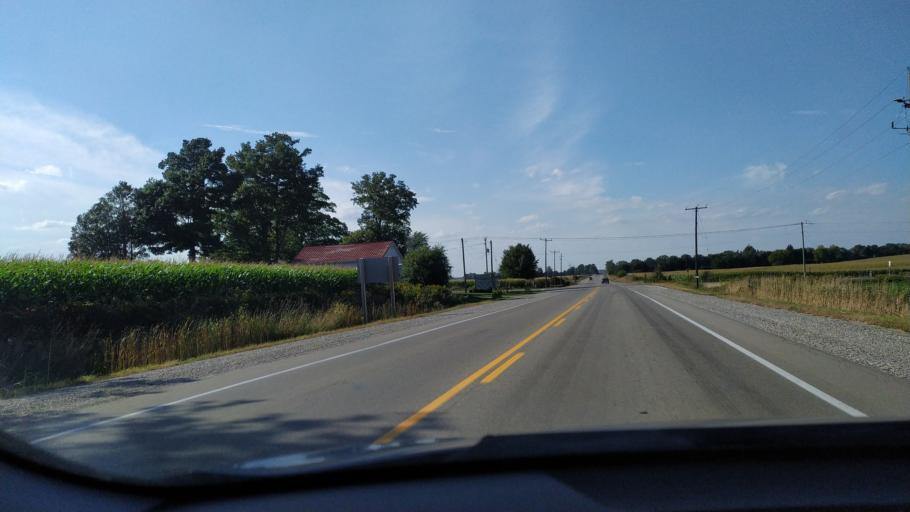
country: CA
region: Ontario
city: Ingersoll
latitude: 43.0540
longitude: -80.8261
